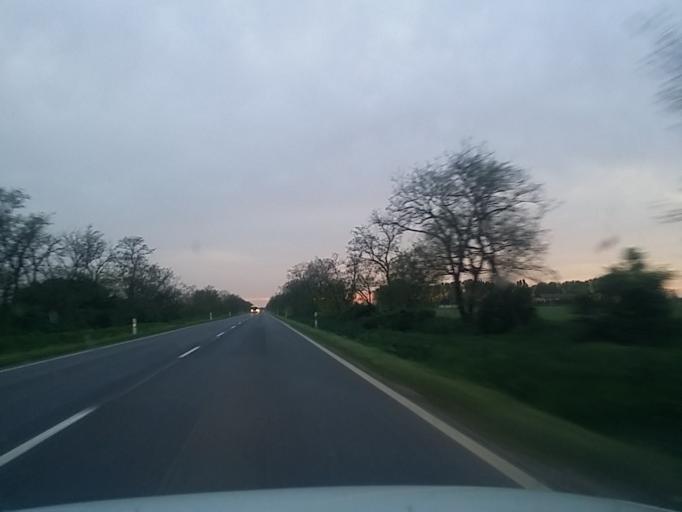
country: HU
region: Bekes
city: Mezobereny
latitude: 46.7107
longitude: 20.9718
